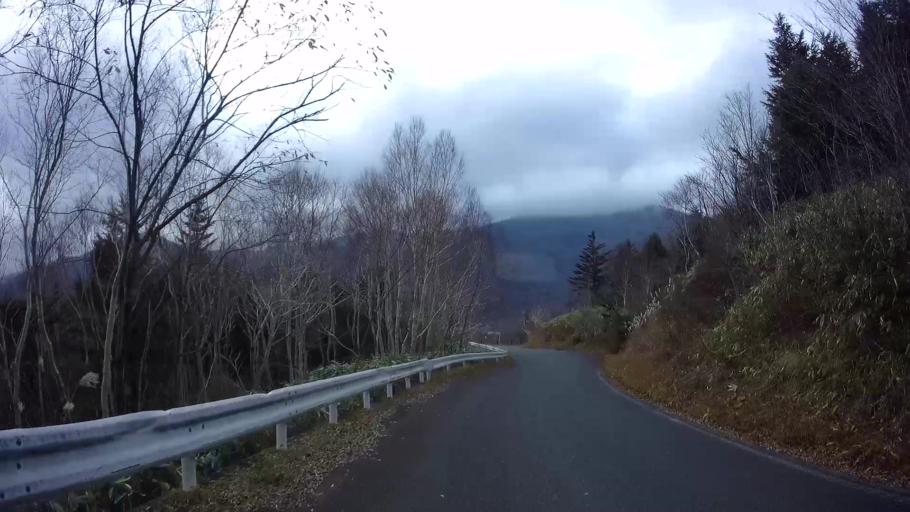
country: JP
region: Gunma
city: Nakanojomachi
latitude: 36.7176
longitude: 138.6486
